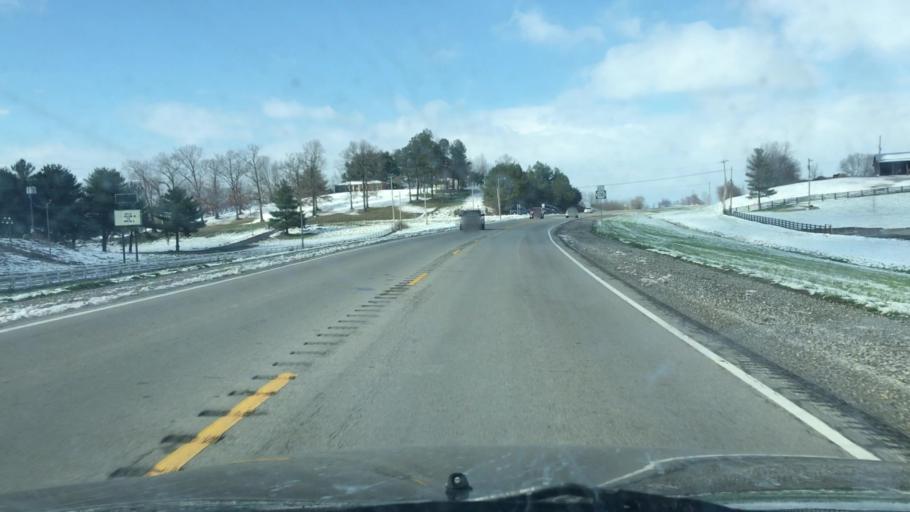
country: US
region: Kentucky
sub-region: Marion County
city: Lebanon
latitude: 37.5380
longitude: -85.3060
